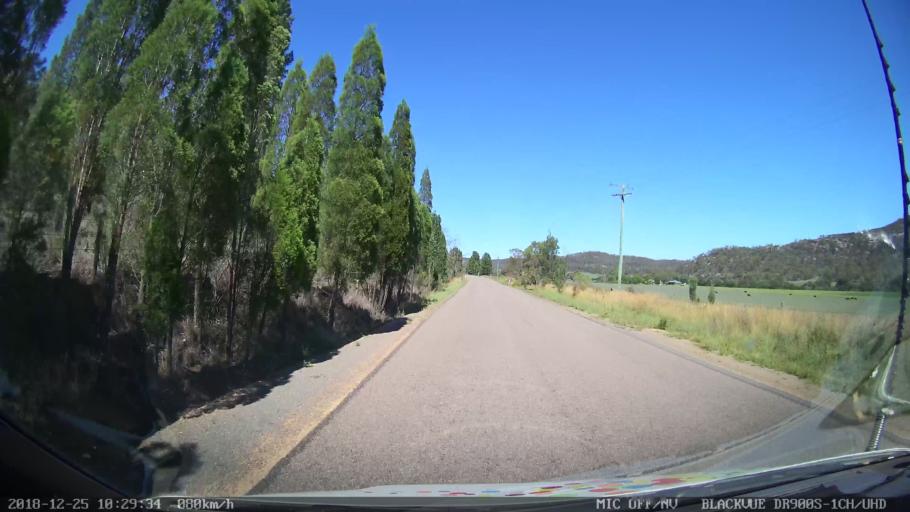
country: AU
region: New South Wales
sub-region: Muswellbrook
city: Denman
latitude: -32.3797
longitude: 150.4494
